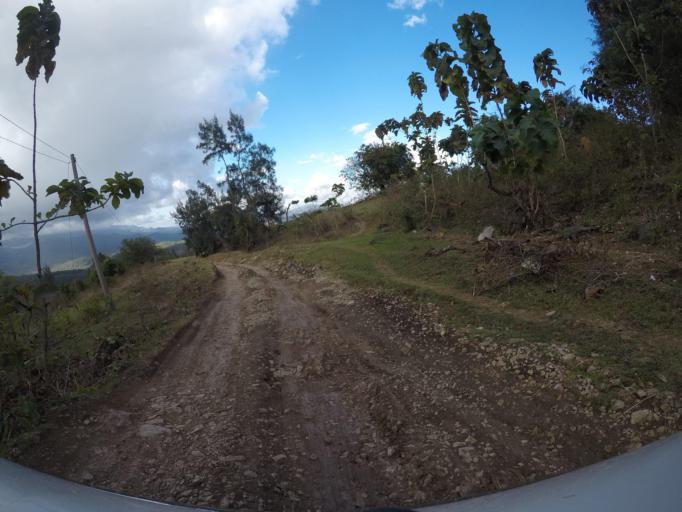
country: TL
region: Baucau
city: Venilale
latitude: -8.6869
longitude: 126.6632
